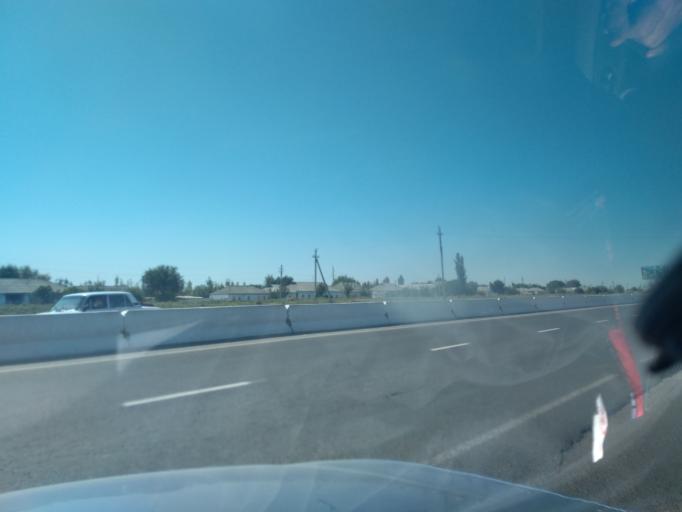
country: UZ
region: Sirdaryo
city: Guliston
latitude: 40.4917
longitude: 68.7000
